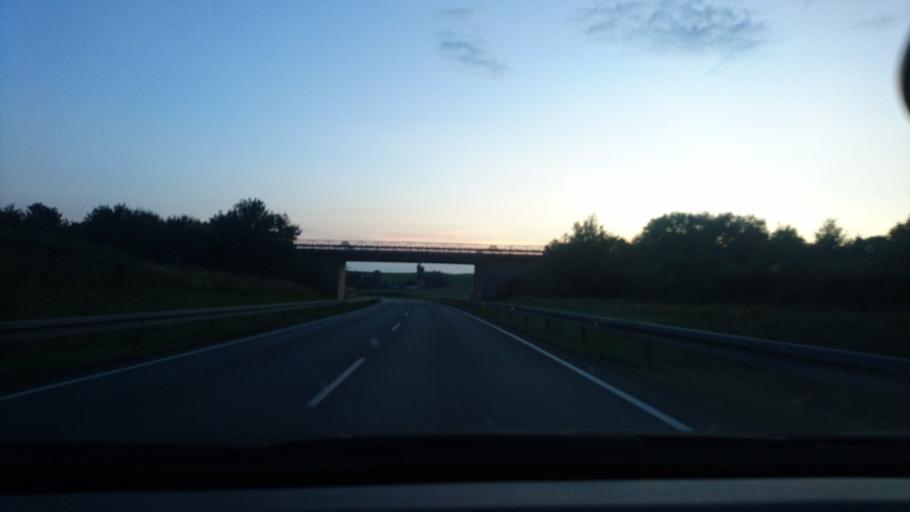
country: DE
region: Bavaria
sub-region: Upper Franconia
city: Selbitz
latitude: 50.3359
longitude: 11.7620
